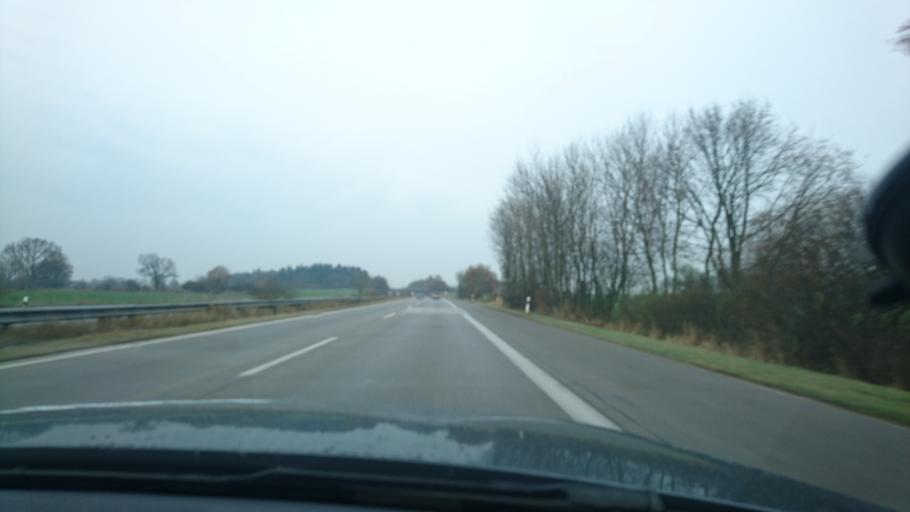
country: DE
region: Schleswig-Holstein
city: Ratekau
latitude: 53.9840
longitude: 10.7336
